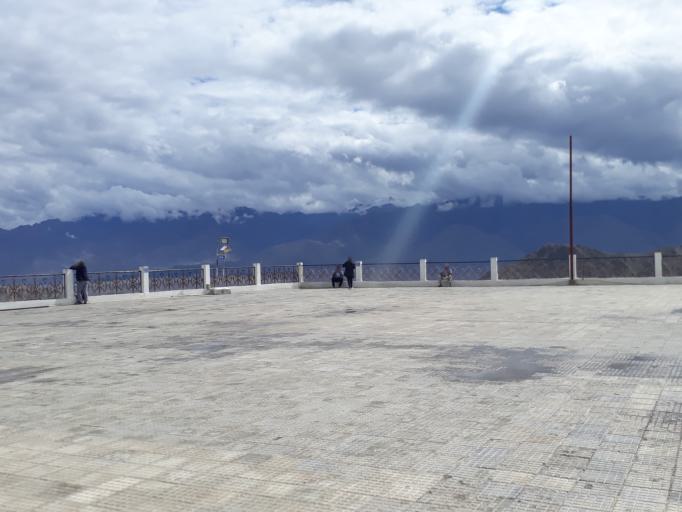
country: IN
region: Kashmir
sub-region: Ladakh
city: Leh
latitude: 34.1737
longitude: 77.5752
